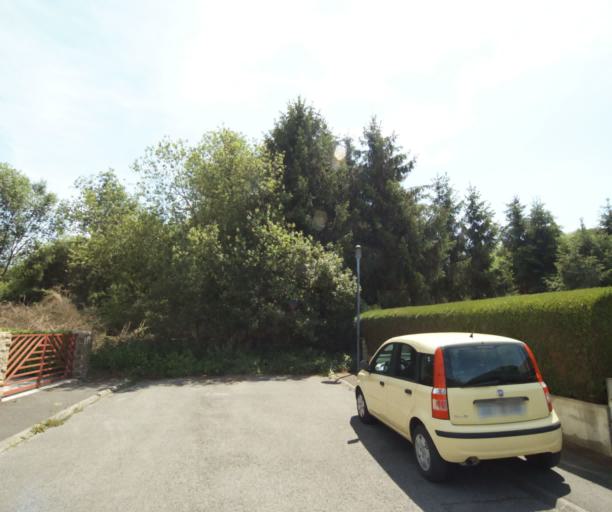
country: FR
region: Champagne-Ardenne
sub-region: Departement des Ardennes
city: Prix-les-Mezieres
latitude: 49.7494
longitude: 4.7065
